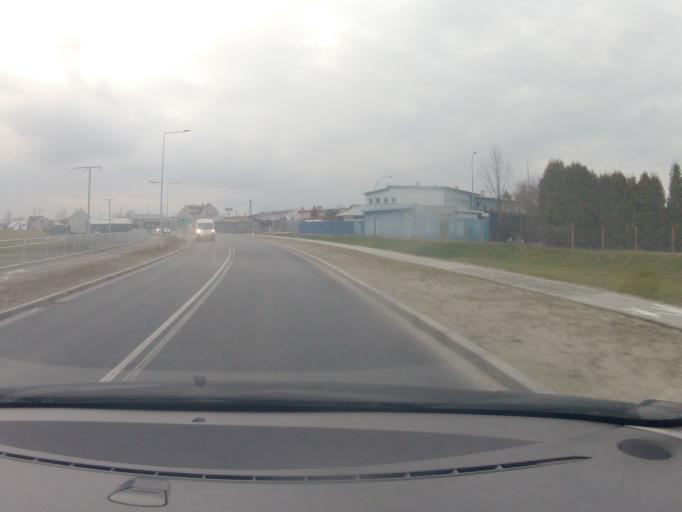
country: PL
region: Subcarpathian Voivodeship
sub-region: Powiat jasielski
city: Jaslo
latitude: 49.7512
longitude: 21.4771
